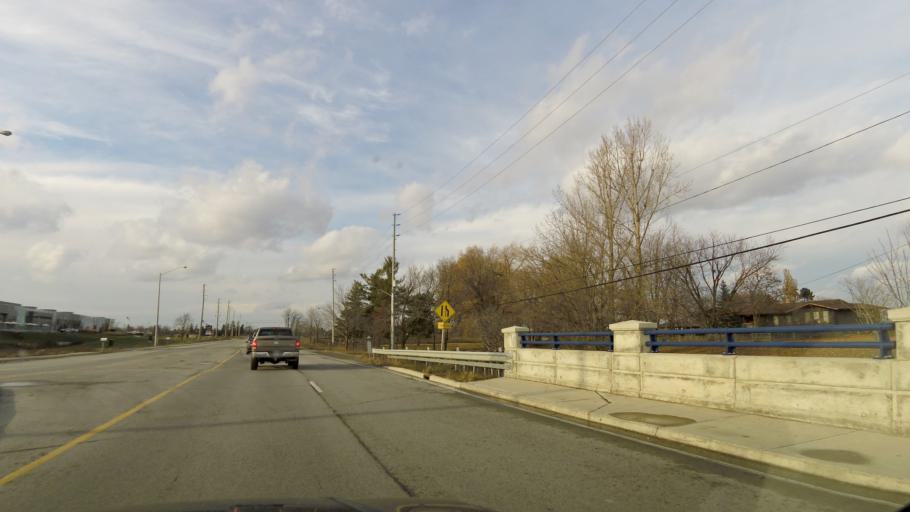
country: CA
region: Ontario
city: Brampton
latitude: 43.7935
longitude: -79.6920
